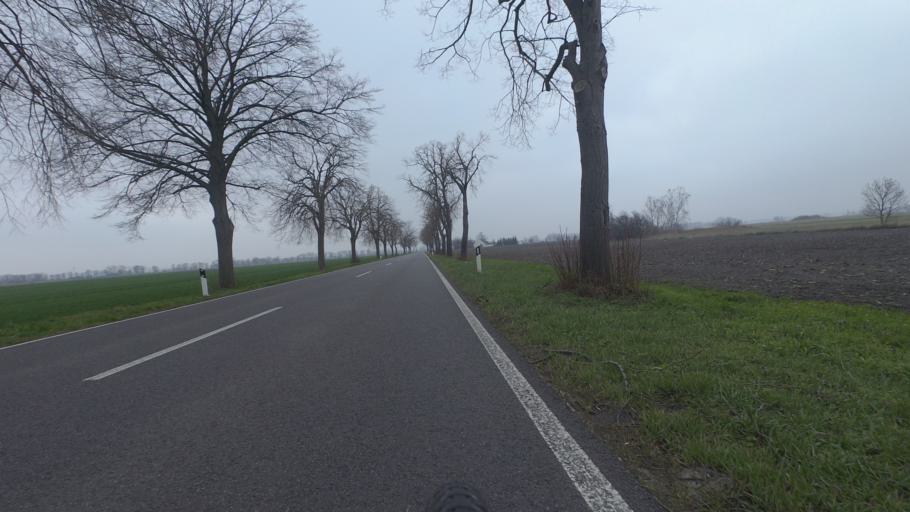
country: DE
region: Brandenburg
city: Nauen
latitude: 52.6243
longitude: 12.8639
